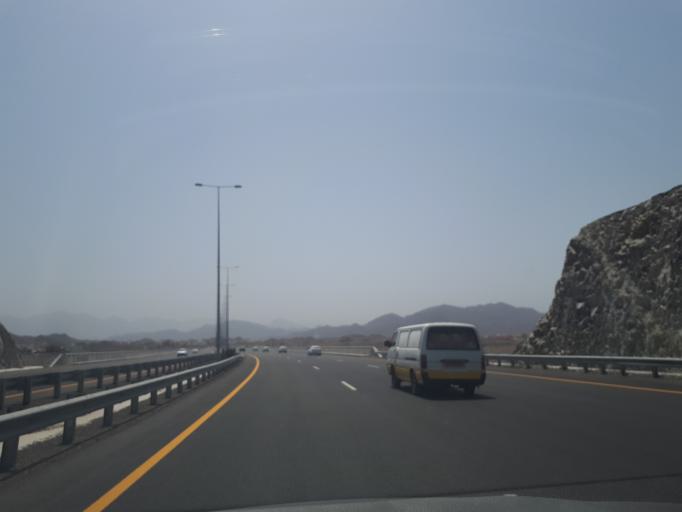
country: OM
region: Muhafazat ad Dakhiliyah
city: Bidbid
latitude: 23.3448
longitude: 58.0976
